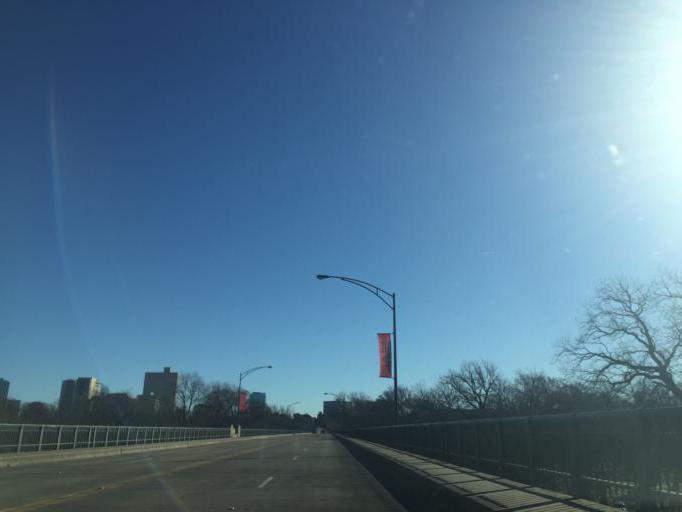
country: US
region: Texas
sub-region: Tarrant County
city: Fort Worth
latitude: 32.7472
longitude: -97.3538
